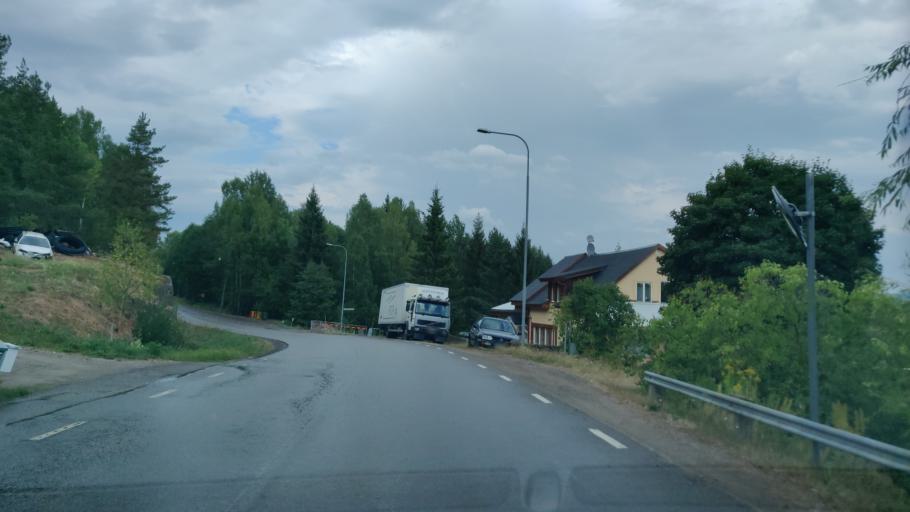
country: SE
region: Vaermland
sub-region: Munkfors Kommun
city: Munkfors
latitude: 59.8440
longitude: 13.5323
